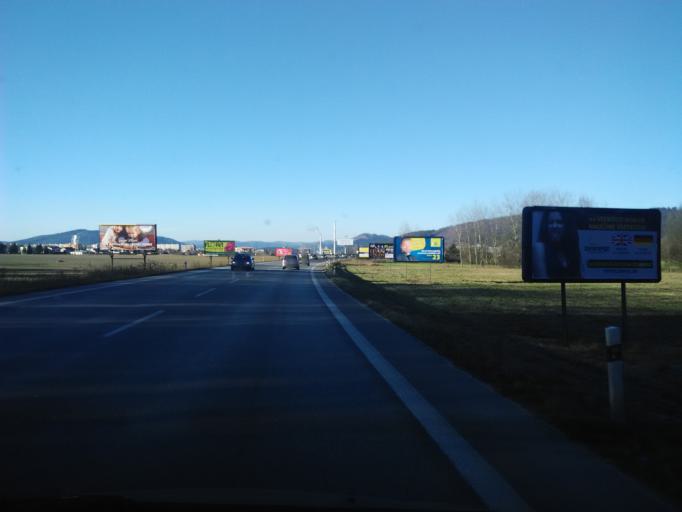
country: SK
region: Zilinsky
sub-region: Okres Zilina
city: Zilina
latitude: 49.2034
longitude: 18.7915
